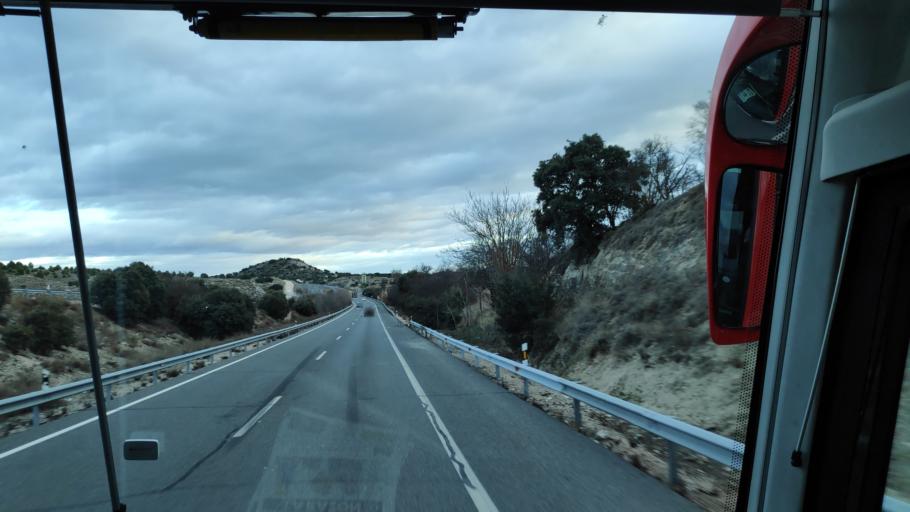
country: ES
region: Madrid
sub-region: Provincia de Madrid
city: Villarejo de Salvanes
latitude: 40.1470
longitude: -3.2180
